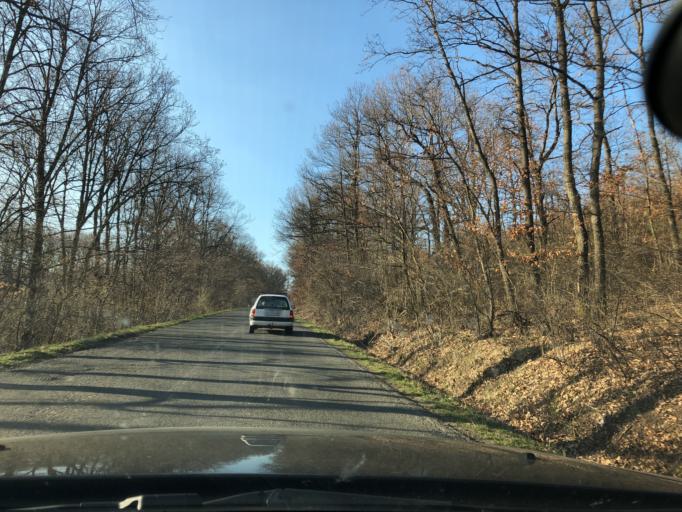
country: HU
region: Nograd
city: Paszto
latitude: 47.9300
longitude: 19.6272
